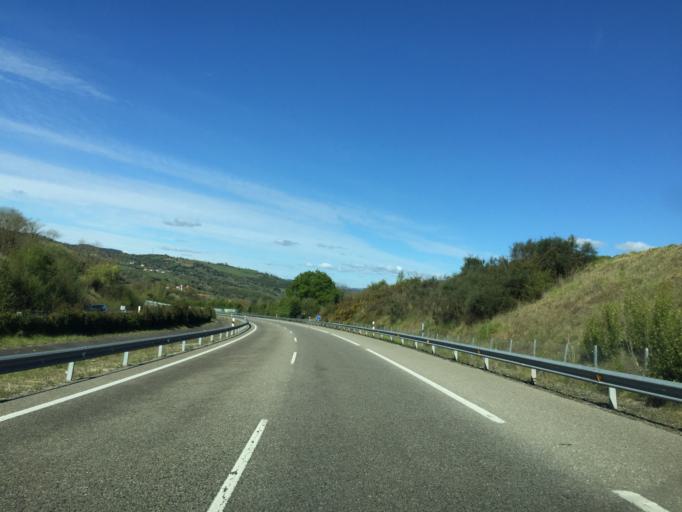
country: ES
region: Asturias
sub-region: Province of Asturias
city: Oviedo
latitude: 43.3533
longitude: -5.9127
